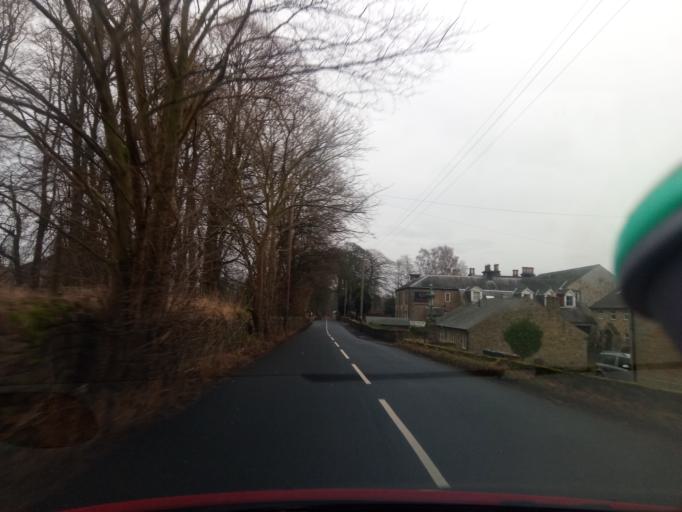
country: GB
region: England
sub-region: Northumberland
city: Birtley
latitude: 55.1453
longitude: -2.2656
